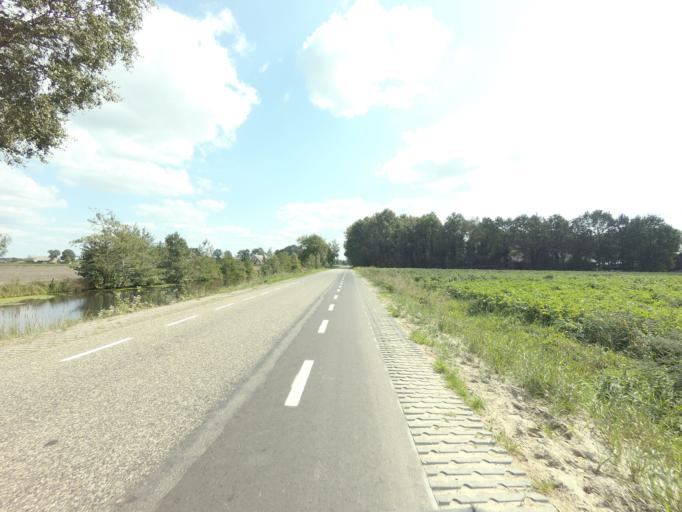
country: NL
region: Drenthe
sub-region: Gemeente Westerveld
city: Dwingeloo
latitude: 52.8652
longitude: 6.4569
